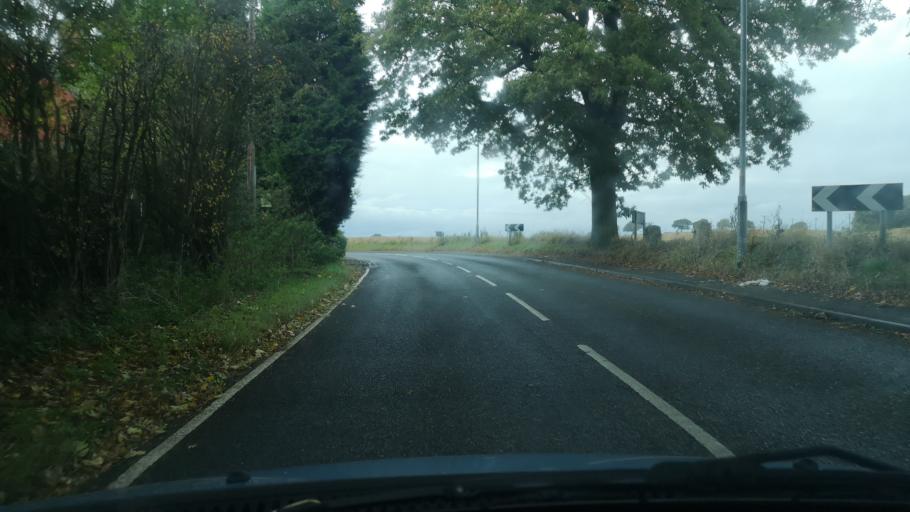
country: GB
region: England
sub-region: City and Borough of Wakefield
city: Low Ackworth
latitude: 53.6605
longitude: -1.3409
